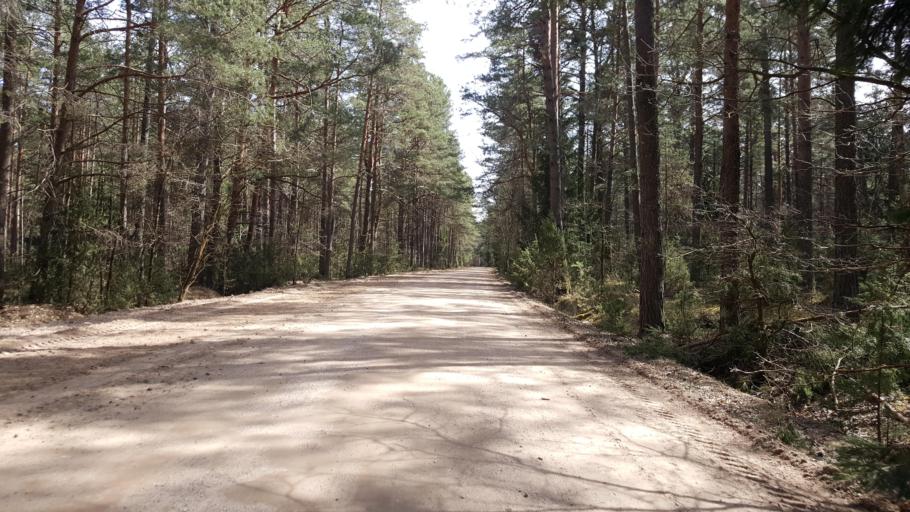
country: BY
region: Brest
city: Kamyanyuki
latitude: 52.5725
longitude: 23.7459
